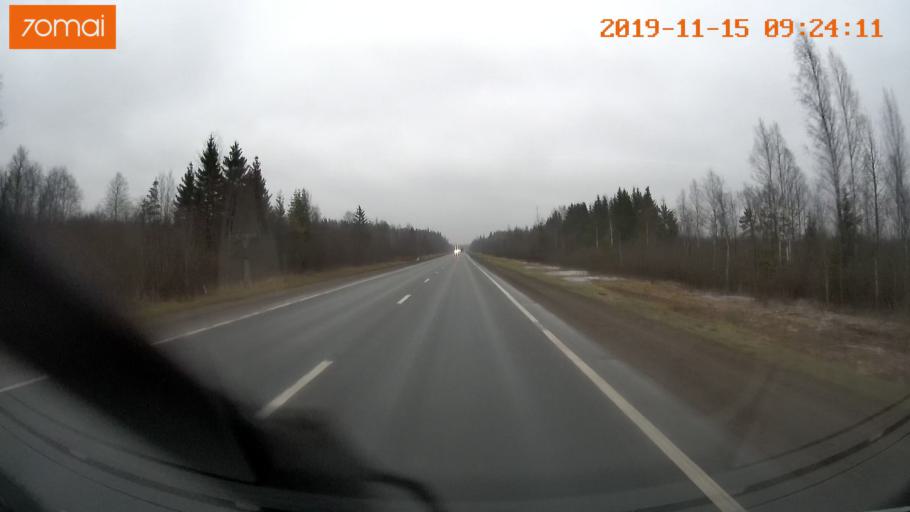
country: RU
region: Vologda
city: Tonshalovo
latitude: 59.3034
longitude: 38.1315
